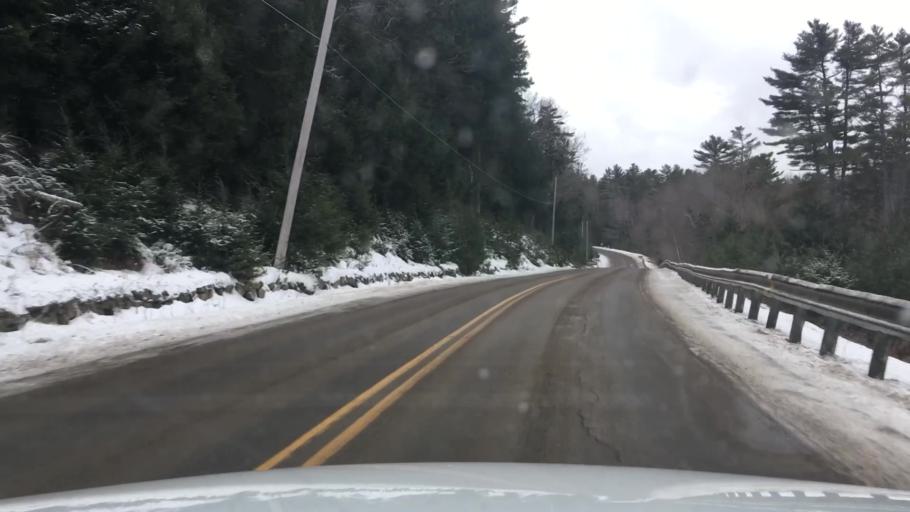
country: US
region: Maine
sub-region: Waldo County
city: Lincolnville
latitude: 44.2876
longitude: -69.0189
